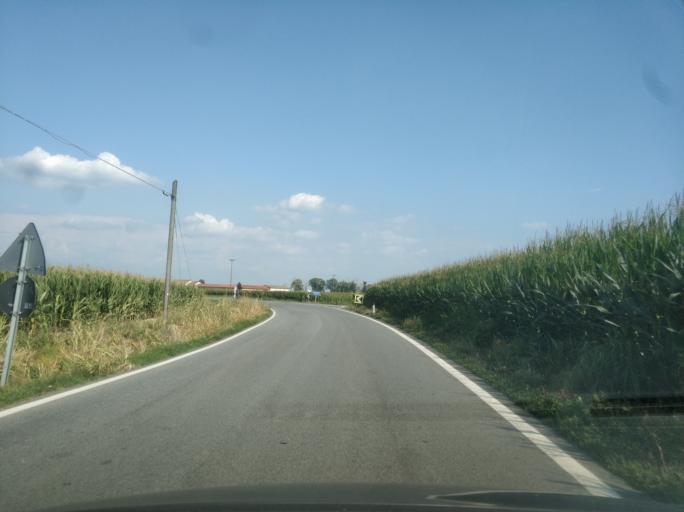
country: IT
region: Piedmont
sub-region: Provincia di Cuneo
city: Centallo
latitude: 44.5314
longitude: 7.6419
